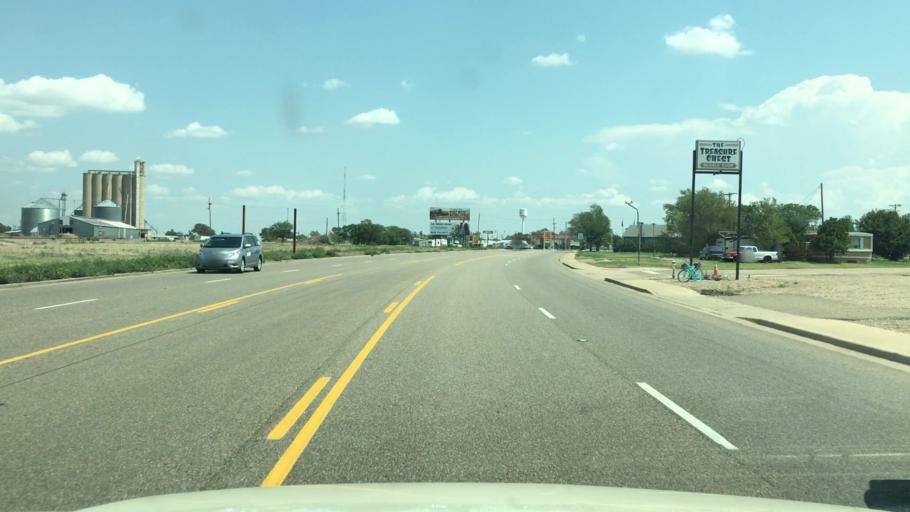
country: US
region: Texas
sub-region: Armstrong County
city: Claude
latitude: 35.1137
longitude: -101.3666
